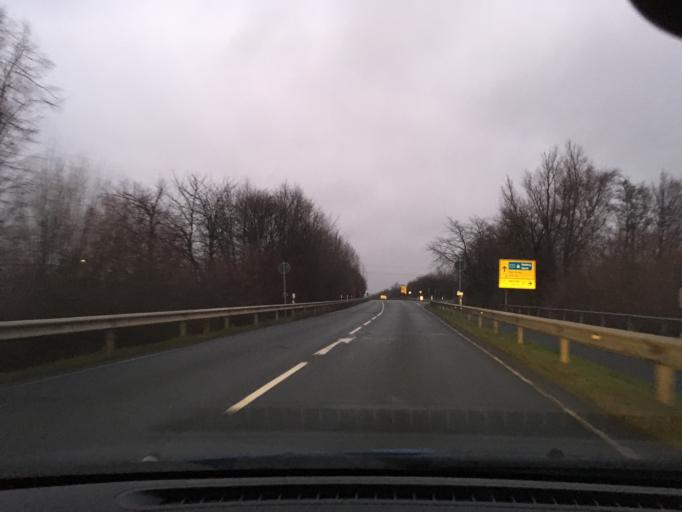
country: DE
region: Lower Saxony
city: Sehnde
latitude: 52.3551
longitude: 9.9060
